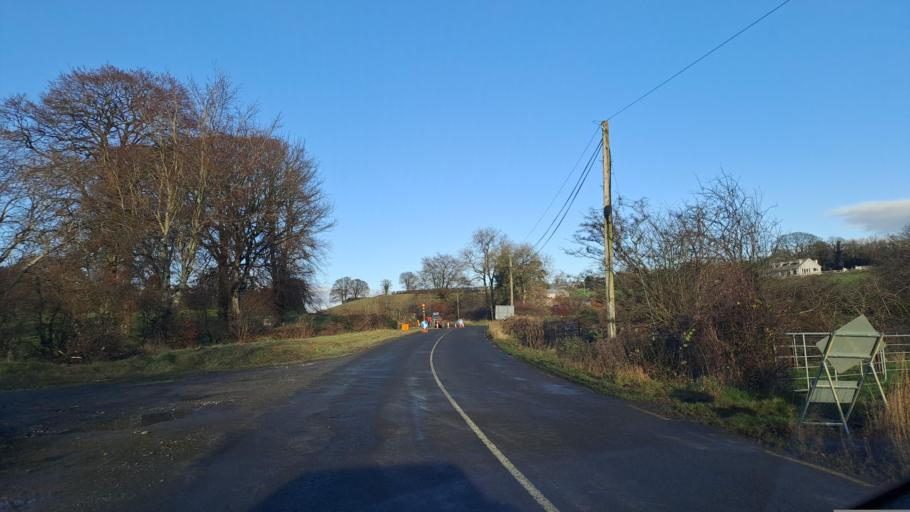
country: IE
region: Ulster
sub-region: An Cabhan
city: Bailieborough
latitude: 53.8982
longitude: -6.9673
